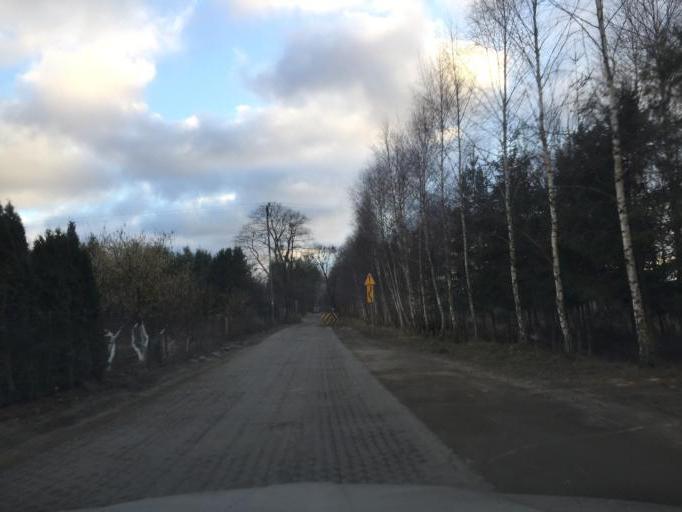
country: PL
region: Pomeranian Voivodeship
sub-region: Powiat kartuski
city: Chwaszczyno
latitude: 54.4104
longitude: 18.4441
